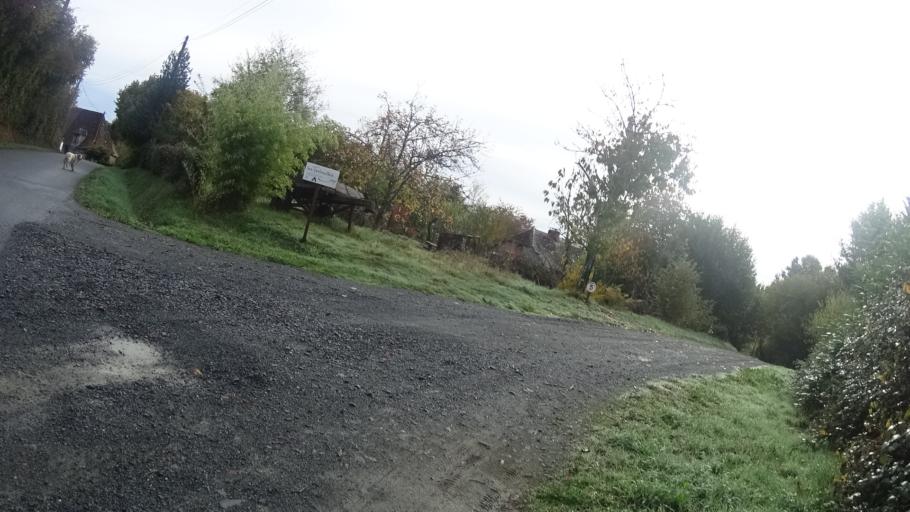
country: FR
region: Aquitaine
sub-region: Departement de la Dordogne
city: Payzac
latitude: 45.3604
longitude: 1.2098
